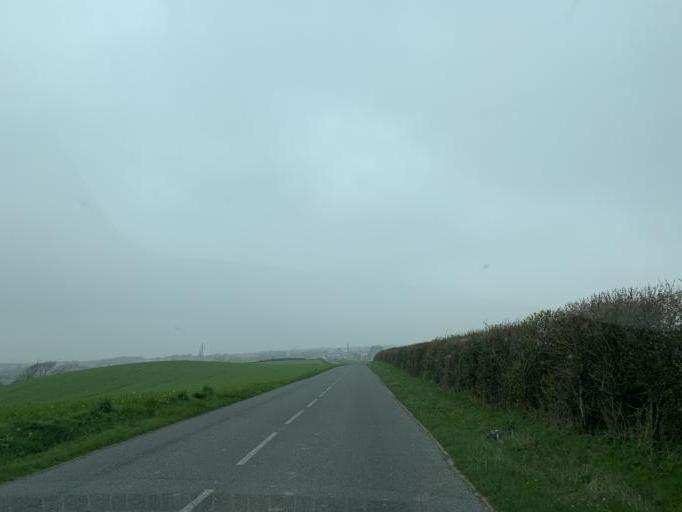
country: FR
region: Nord-Pas-de-Calais
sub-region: Departement du Pas-de-Calais
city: Marquise
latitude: 50.8021
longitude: 1.7117
